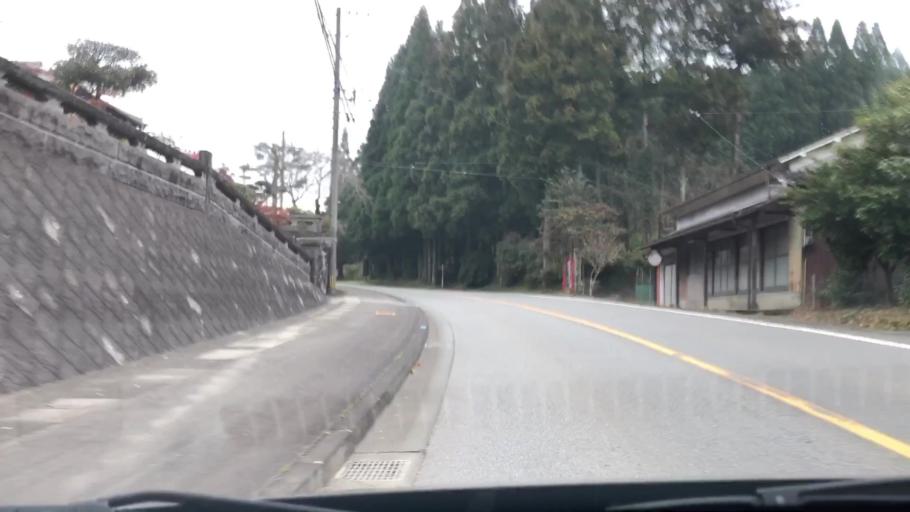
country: JP
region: Oita
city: Usuki
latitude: 33.0055
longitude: 131.6498
